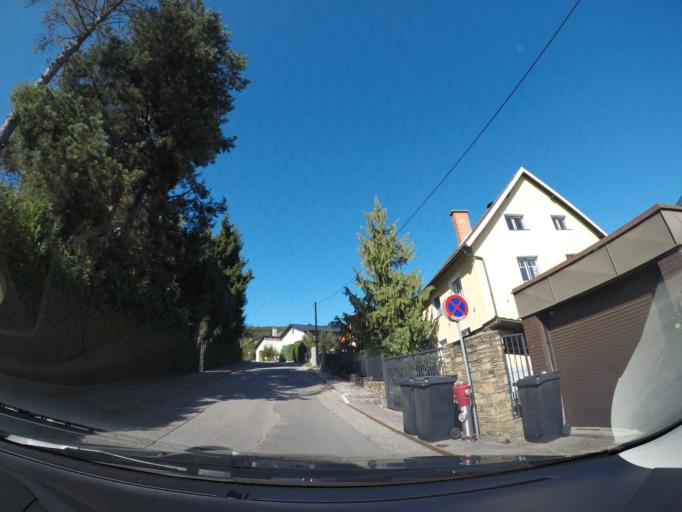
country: AT
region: Lower Austria
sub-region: Politischer Bezirk Wien-Umgebung
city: Pressbaum
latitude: 48.1879
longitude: 16.1040
